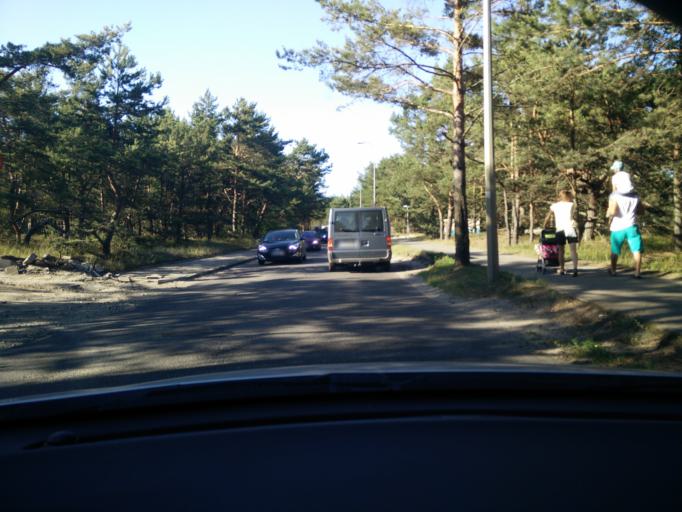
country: PL
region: Pomeranian Voivodeship
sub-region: Powiat pucki
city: Hel
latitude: 54.6156
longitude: 18.8033
